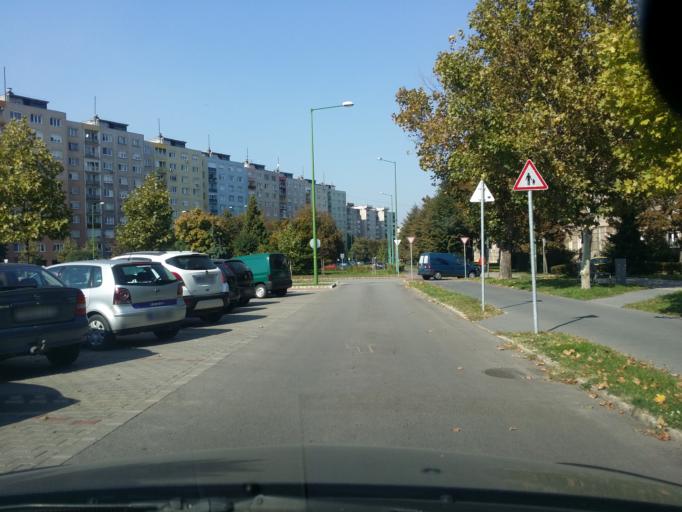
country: HU
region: Fejer
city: Dunaujvaros
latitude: 46.9657
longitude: 18.9394
